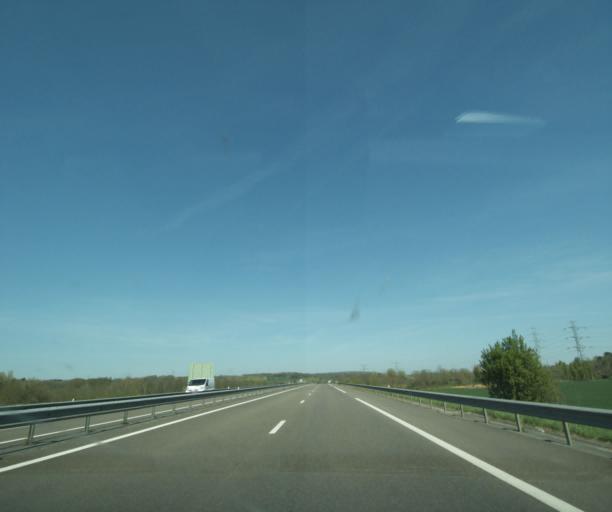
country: FR
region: Bourgogne
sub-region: Departement de la Nievre
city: Coulanges-les-Nevers
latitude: 47.0005
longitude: 3.2053
